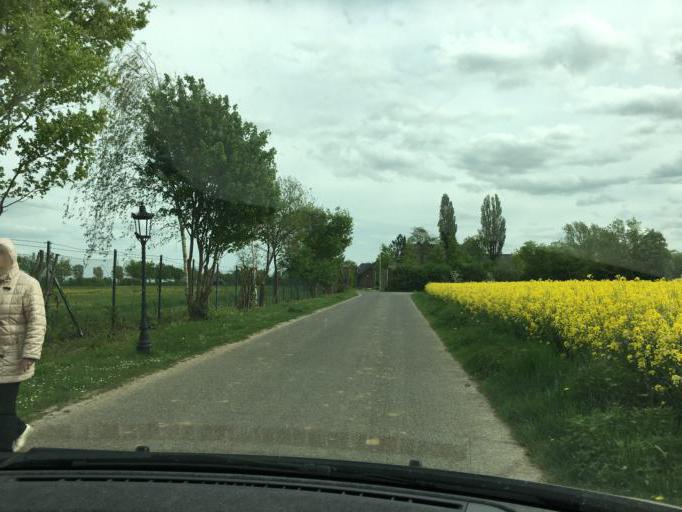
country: DE
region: North Rhine-Westphalia
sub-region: Regierungsbezirk Koln
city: Merzenich
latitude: 50.7931
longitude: 6.5433
